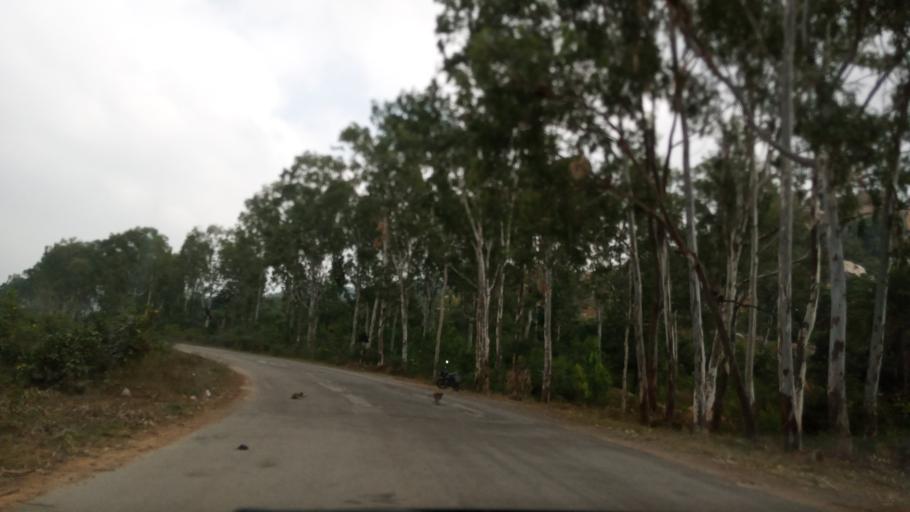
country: IN
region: Andhra Pradesh
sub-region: Chittoor
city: Madanapalle
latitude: 13.5043
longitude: 78.3338
